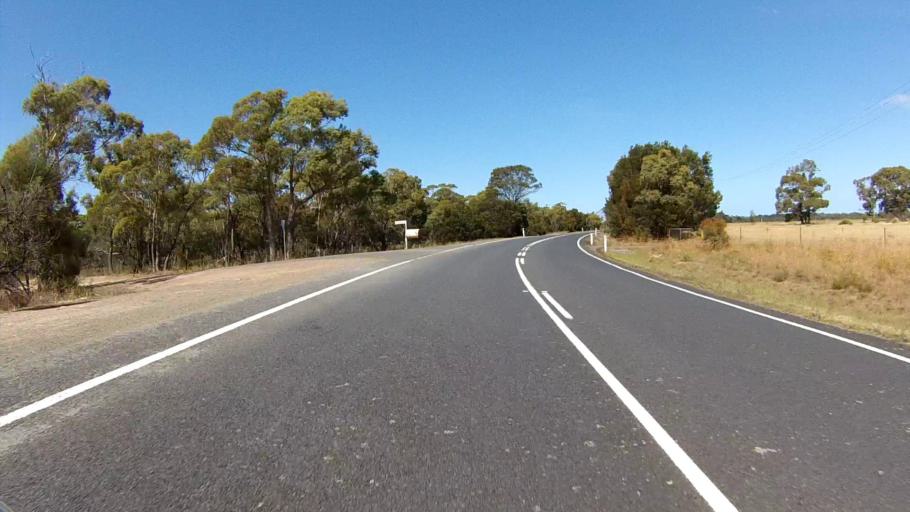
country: AU
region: Tasmania
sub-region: Break O'Day
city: St Helens
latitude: -42.0536
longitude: 148.0566
